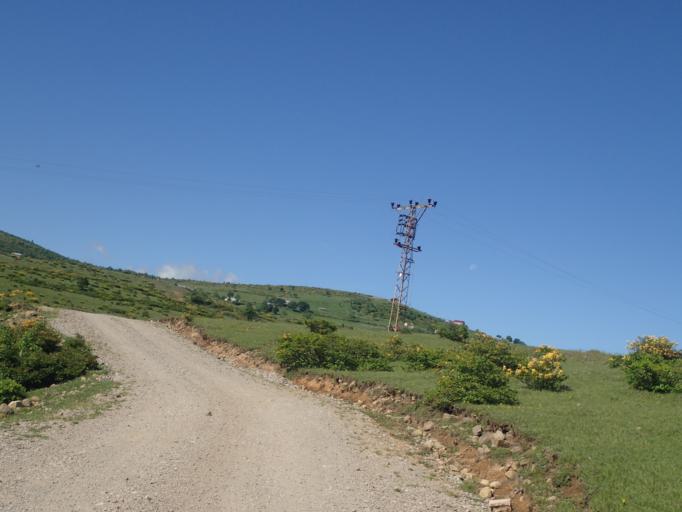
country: TR
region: Ordu
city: Topcam
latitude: 40.6766
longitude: 37.9288
